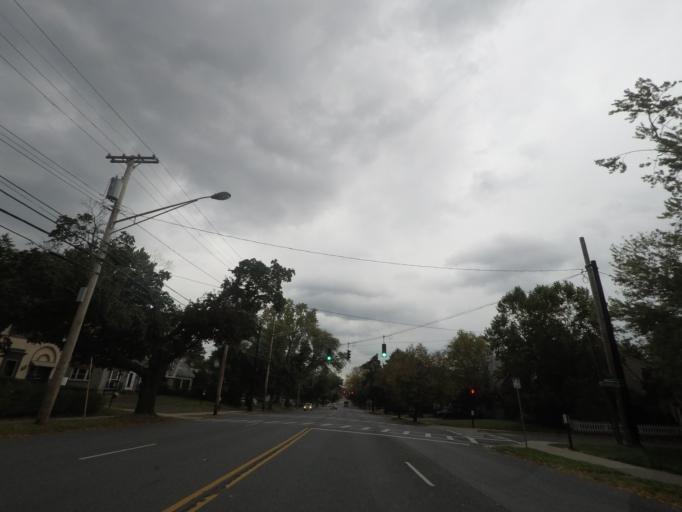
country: US
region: New York
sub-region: Albany County
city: Roessleville
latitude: 42.6702
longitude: -73.8034
